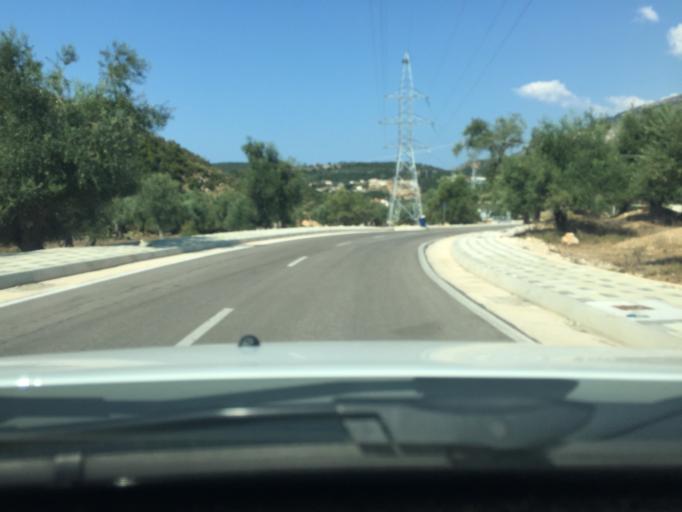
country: AL
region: Vlore
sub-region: Rrethi i Vlores
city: Himare
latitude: 40.1106
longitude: 19.7508
